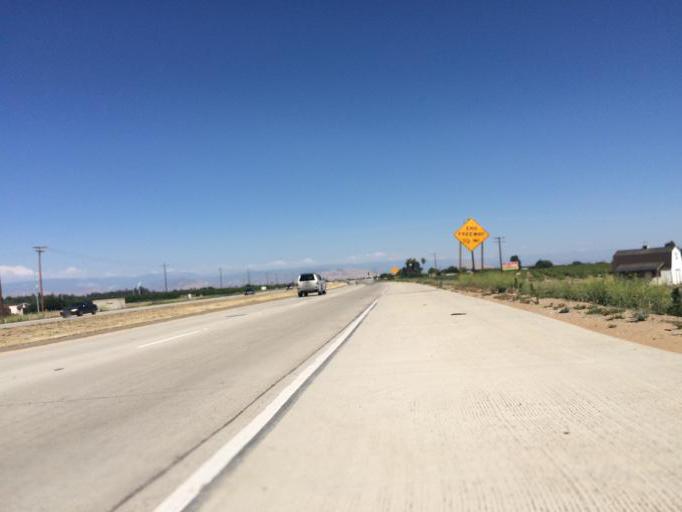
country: US
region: California
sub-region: Fresno County
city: Sunnyside
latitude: 36.7370
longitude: -119.6563
